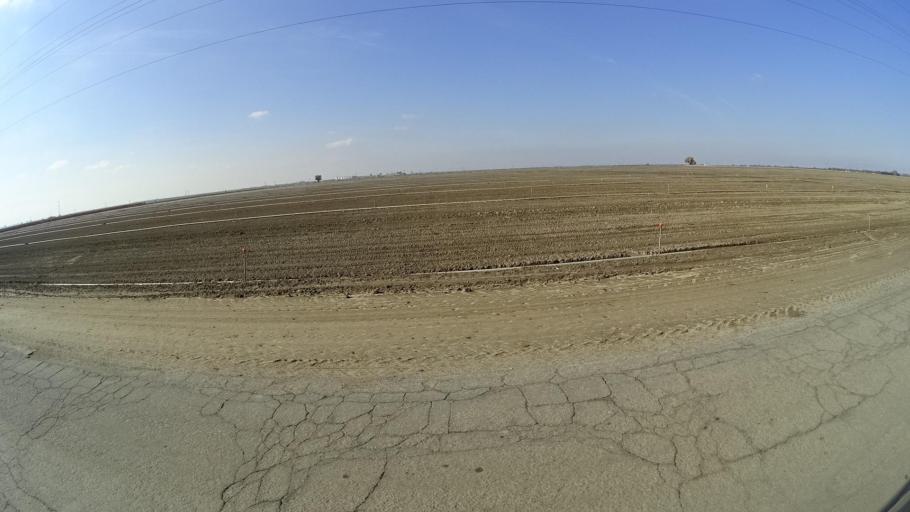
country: US
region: California
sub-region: Kern County
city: Arvin
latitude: 35.2622
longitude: -118.8070
